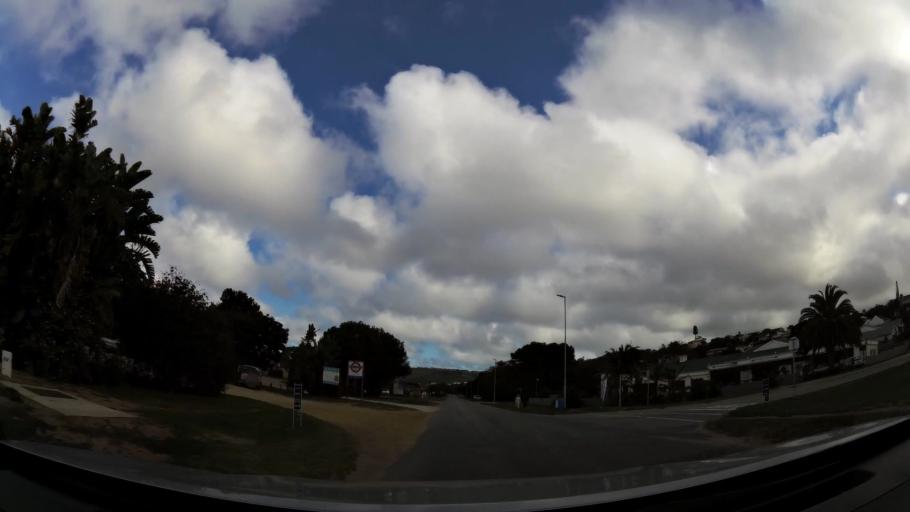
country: ZA
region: Western Cape
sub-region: Eden District Municipality
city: Plettenberg Bay
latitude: -34.0740
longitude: 23.3667
